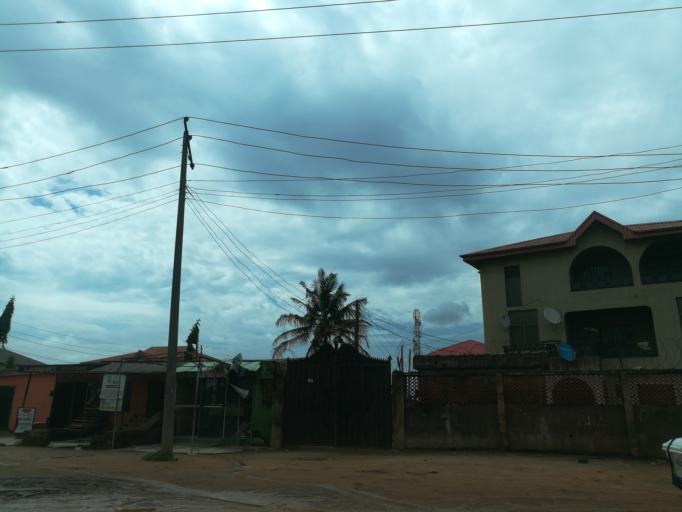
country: NG
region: Lagos
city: Ikorodu
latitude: 6.6335
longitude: 3.5109
